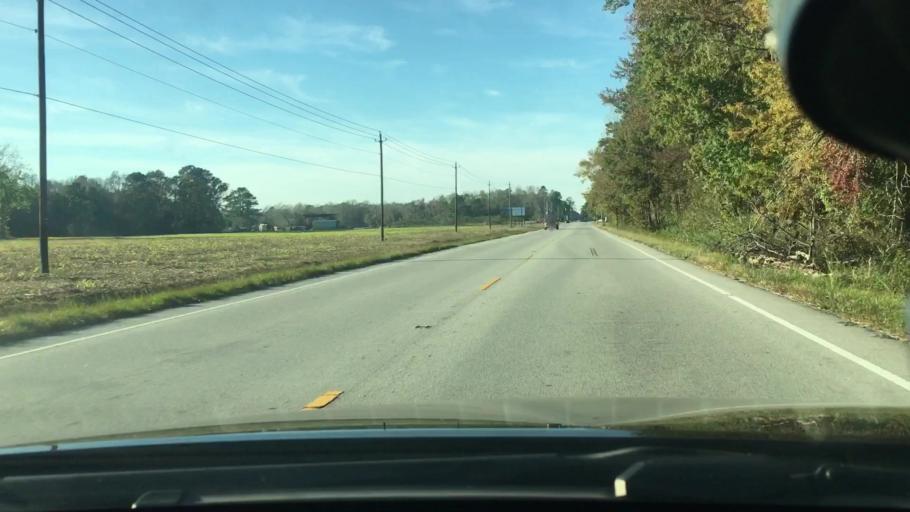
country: US
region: North Carolina
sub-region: Craven County
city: Vanceboro
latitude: 35.2467
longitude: -77.0856
